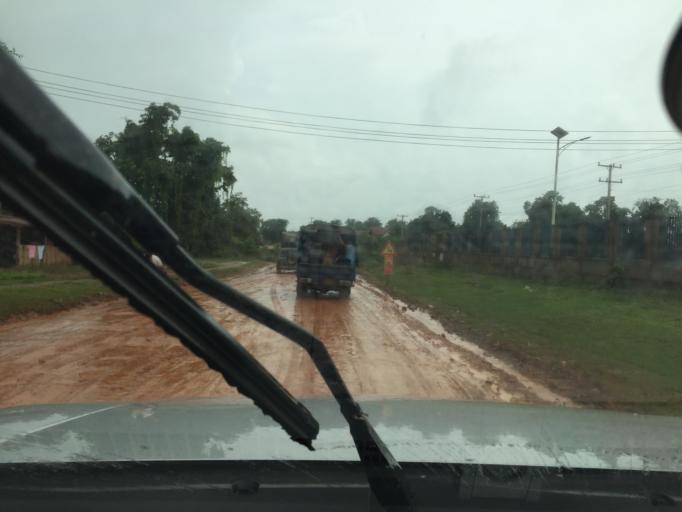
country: LA
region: Attapu
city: Attapu
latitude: 14.8239
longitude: 106.7972
